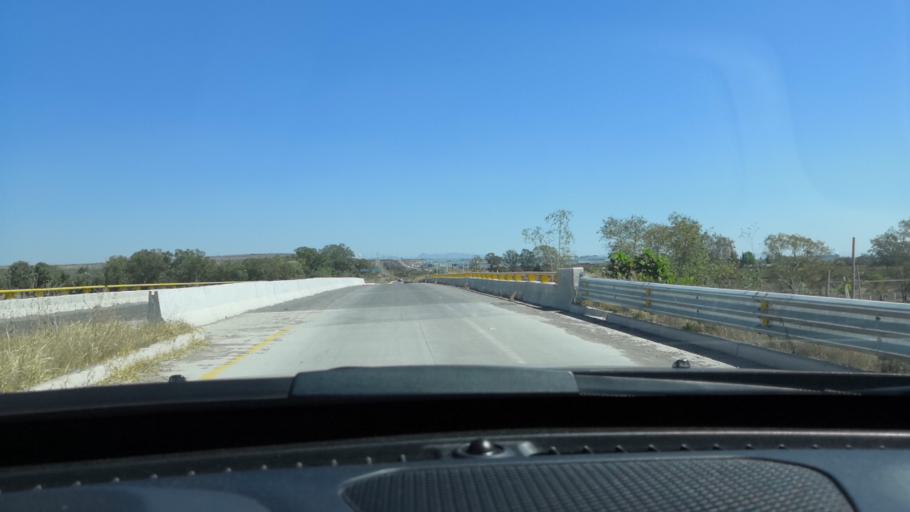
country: MX
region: Guanajuato
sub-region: Leon
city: Centro Familiar la Soledad
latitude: 21.0986
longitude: -101.7800
